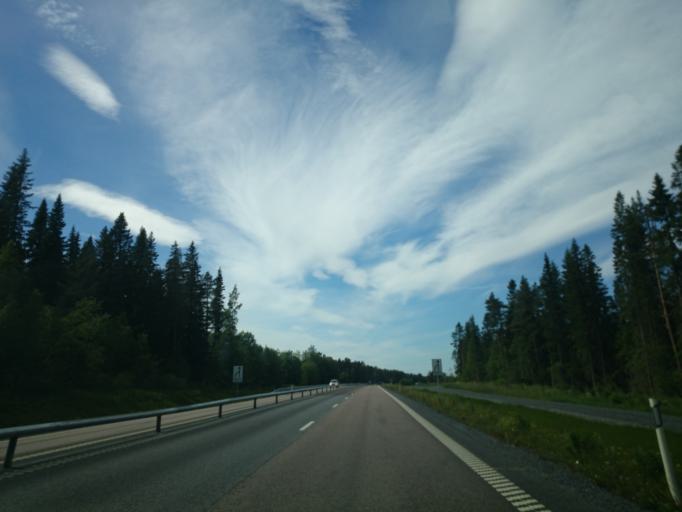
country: SE
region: Jaemtland
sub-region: OEstersunds Kommun
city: Ostersund
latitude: 63.2542
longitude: 14.5707
